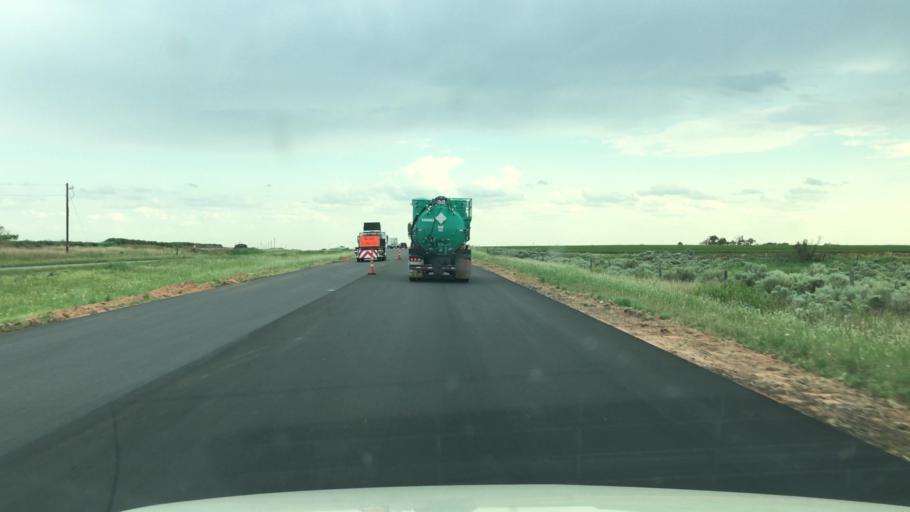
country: US
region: Texas
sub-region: Hall County
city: Memphis
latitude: 34.6343
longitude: -100.4767
